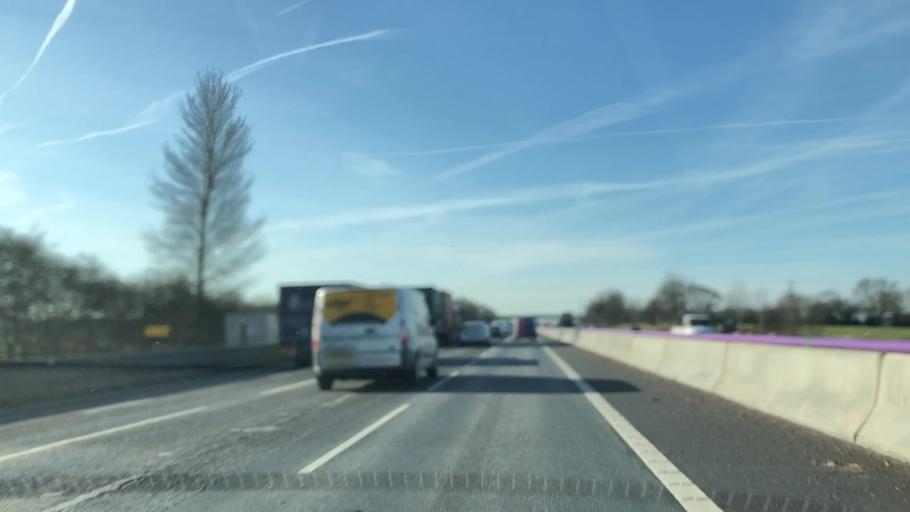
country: GB
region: England
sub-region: Cheshire East
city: Alsager
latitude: 53.1063
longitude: -2.3392
